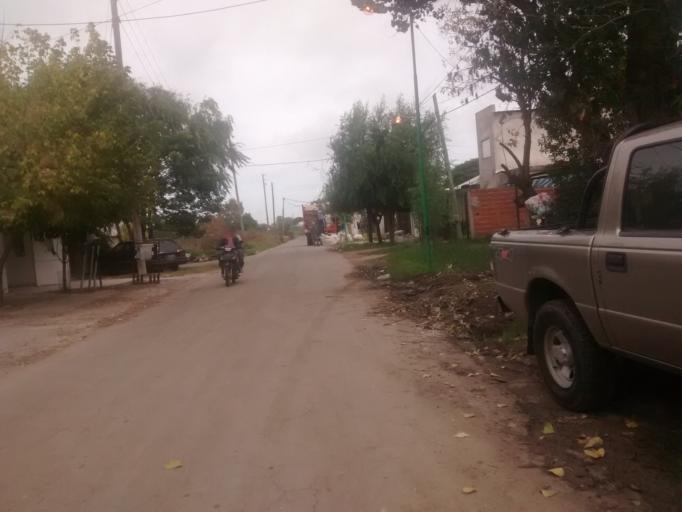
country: AR
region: Buenos Aires
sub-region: Partido de La Plata
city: La Plata
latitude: -34.9360
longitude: -57.9121
